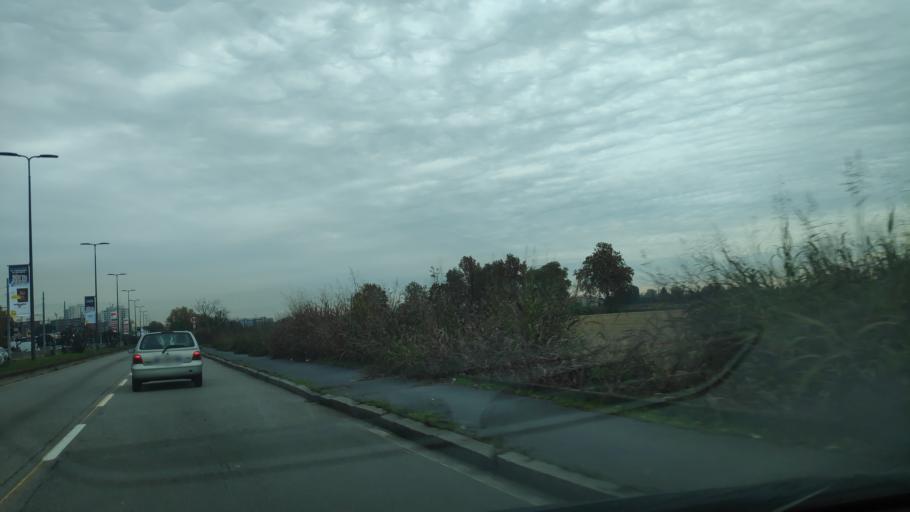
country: IT
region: Lombardy
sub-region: Citta metropolitana di Milano
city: Rozzano
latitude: 45.3961
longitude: 9.1733
